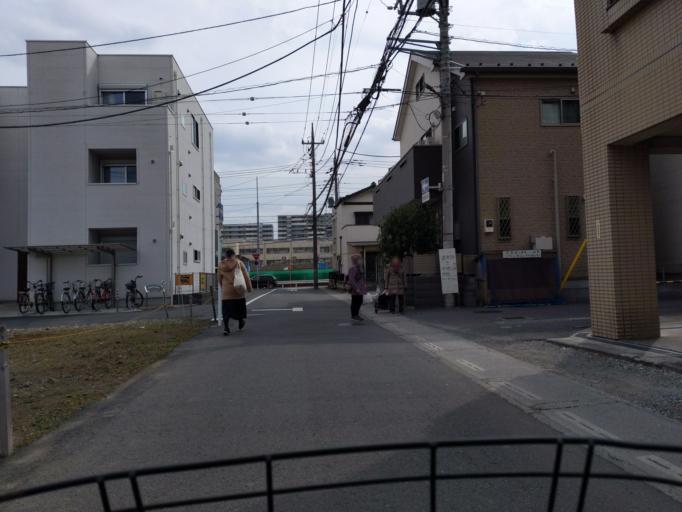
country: JP
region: Saitama
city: Soka
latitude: 35.8462
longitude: 139.7975
